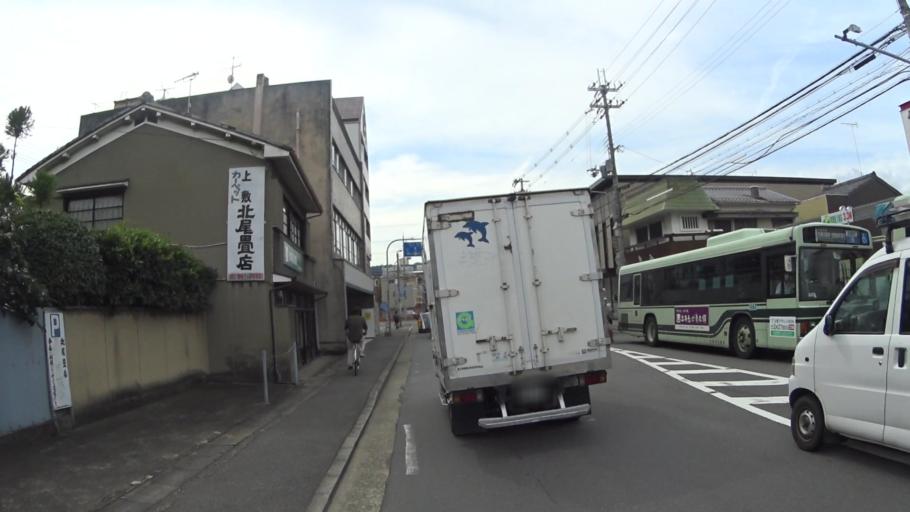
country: JP
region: Kyoto
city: Muko
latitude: 35.0037
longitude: 135.7070
